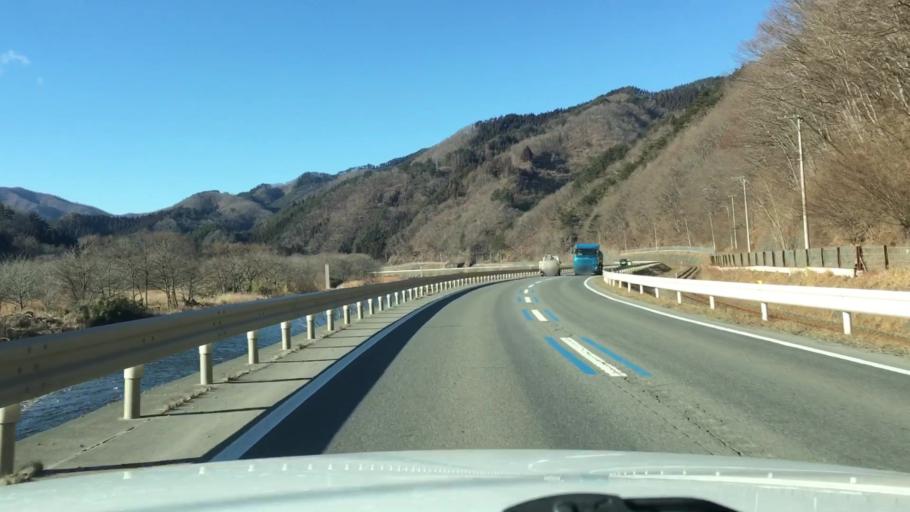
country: JP
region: Iwate
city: Miyako
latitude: 39.6304
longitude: 141.8545
